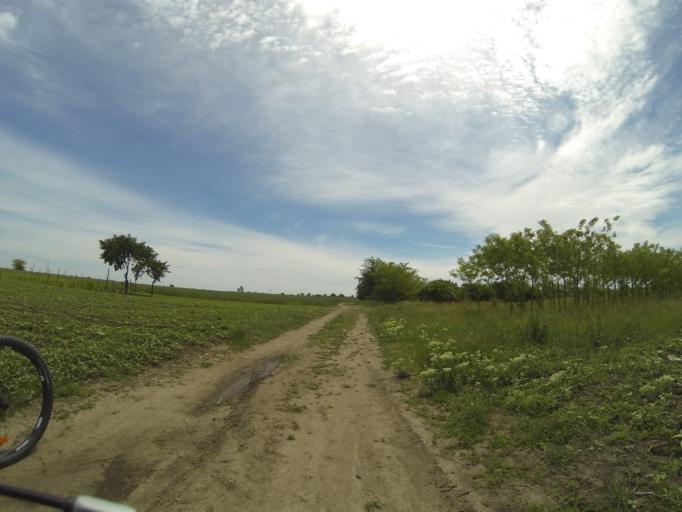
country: RO
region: Dolj
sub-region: Comuna Leu
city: Leu
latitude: 44.2017
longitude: 23.9972
